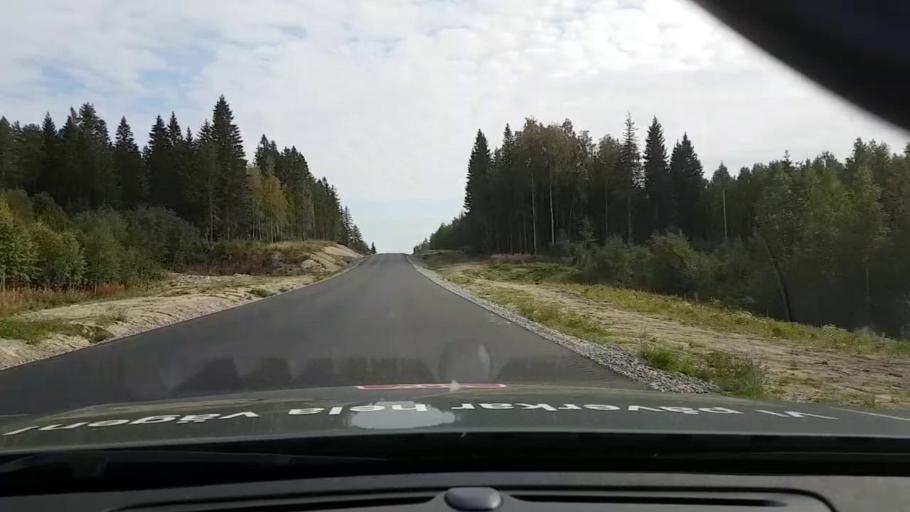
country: SE
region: Vaesternorrland
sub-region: OErnskoeldsviks Kommun
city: Bjasta
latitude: 63.2923
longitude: 18.5017
